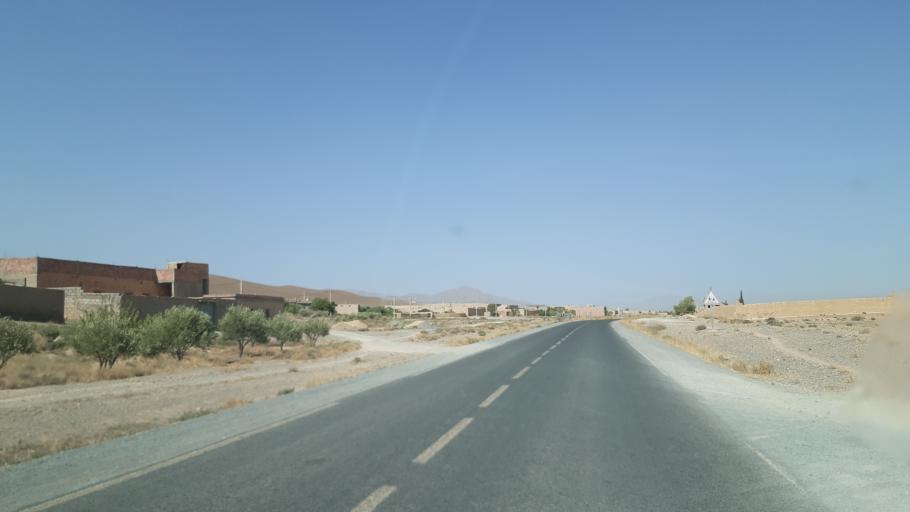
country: MA
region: Meknes-Tafilalet
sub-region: Errachidia
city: Errachidia
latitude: 32.2535
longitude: -4.5674
